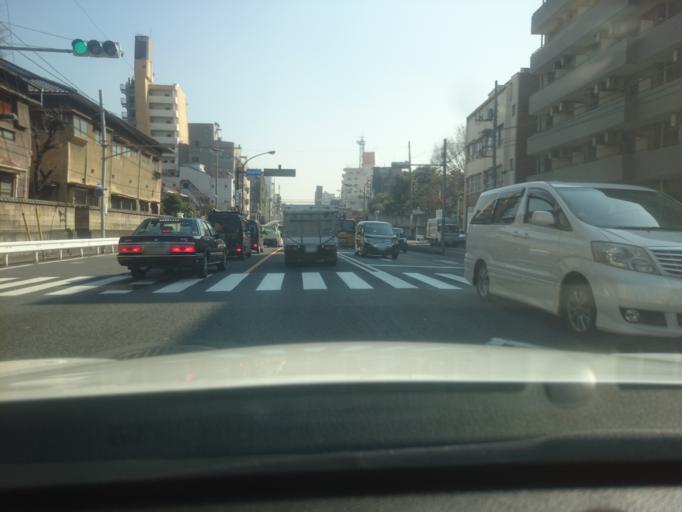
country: JP
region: Tokyo
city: Musashino
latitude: 35.7056
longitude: 139.6157
